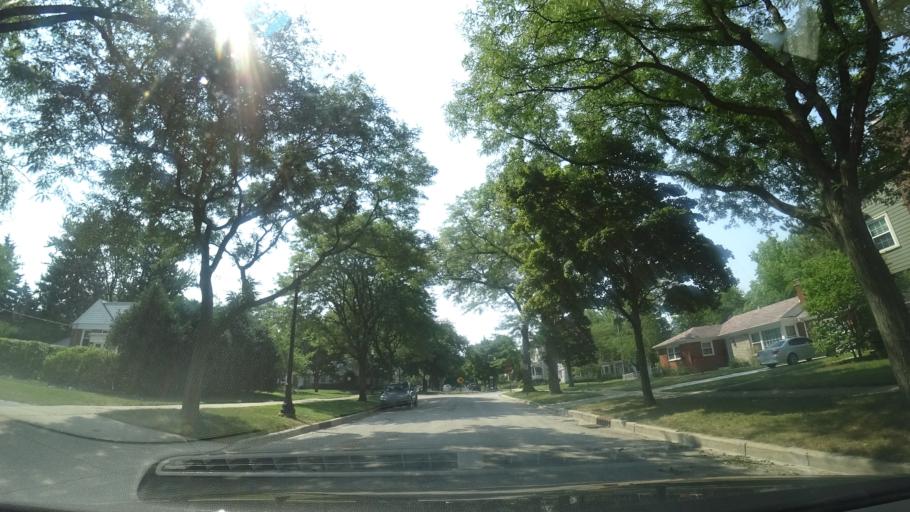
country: US
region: Illinois
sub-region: Cook County
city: Evanston
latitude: 42.0255
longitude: -87.6916
